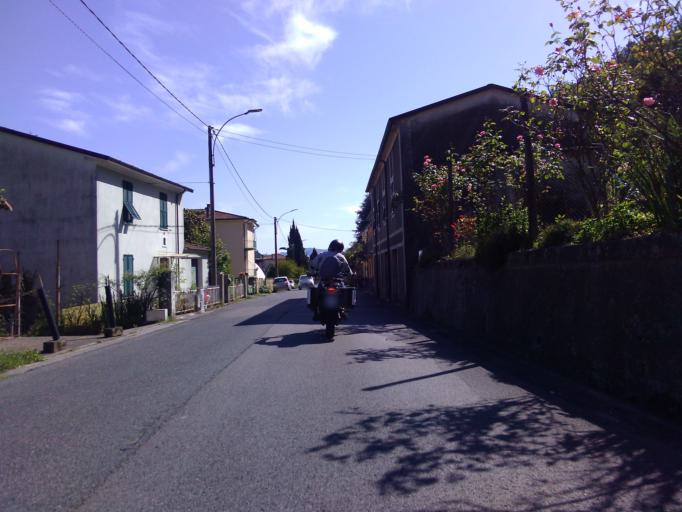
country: IT
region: Tuscany
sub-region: Provincia di Massa-Carrara
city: Licciana Nardi
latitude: 44.2679
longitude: 10.0416
